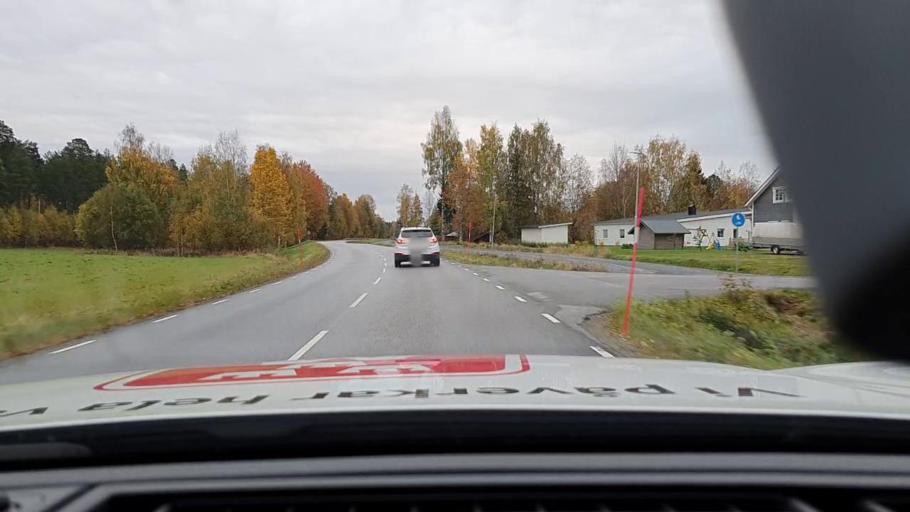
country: SE
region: Norrbotten
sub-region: Bodens Kommun
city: Saevast
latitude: 65.7712
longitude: 21.7023
